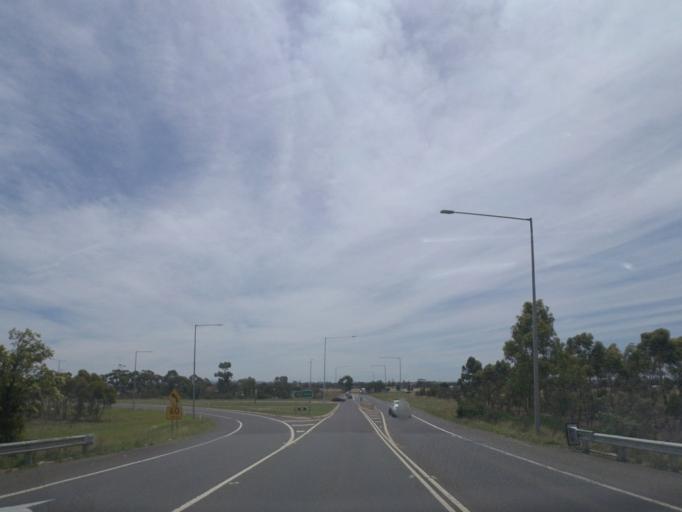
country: AU
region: Victoria
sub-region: Melton
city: Rockbank
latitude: -37.7438
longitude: 144.7006
